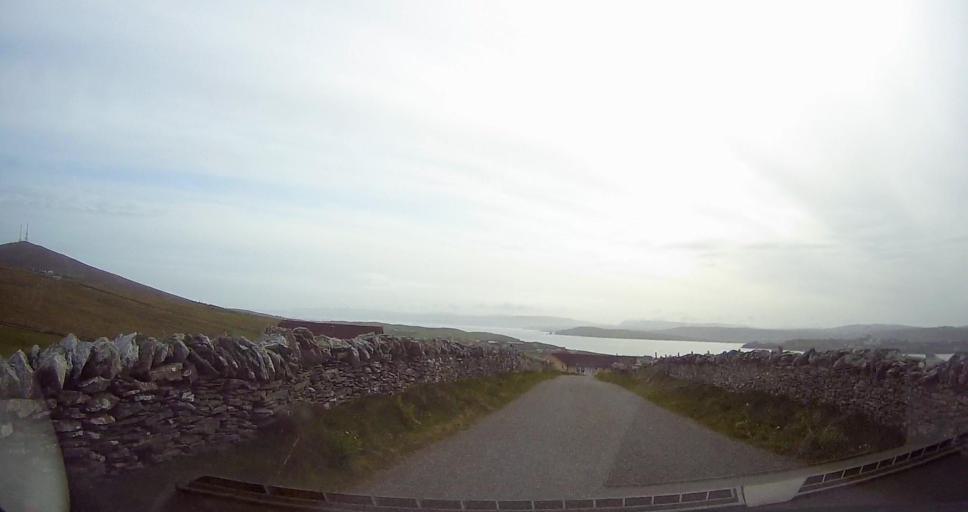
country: GB
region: Scotland
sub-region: Shetland Islands
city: Shetland
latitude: 60.1518
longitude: -1.0977
